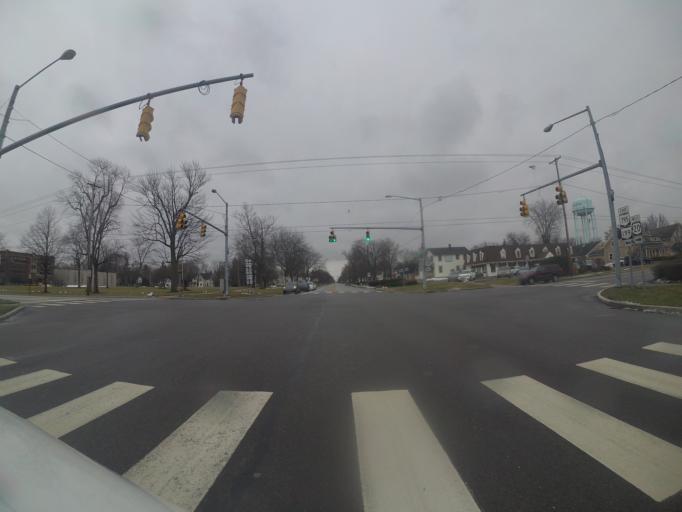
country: US
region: Ohio
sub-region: Wood County
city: Perrysburg
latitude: 41.5573
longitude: -83.6280
